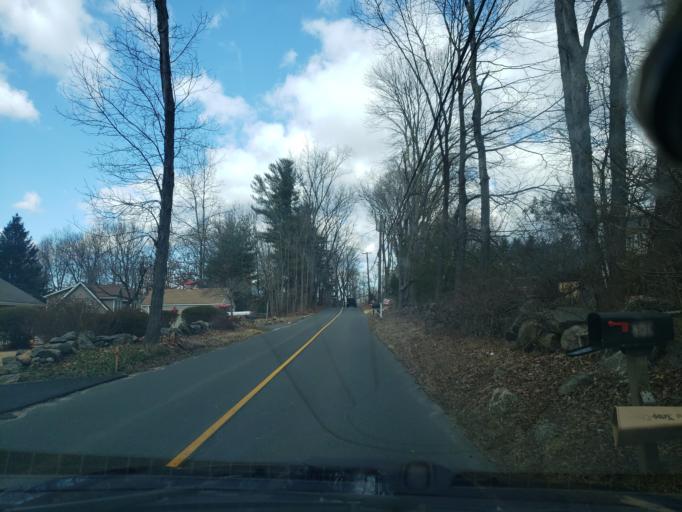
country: US
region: Connecticut
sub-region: Fairfield County
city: Bethel
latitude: 41.3852
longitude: -73.3775
